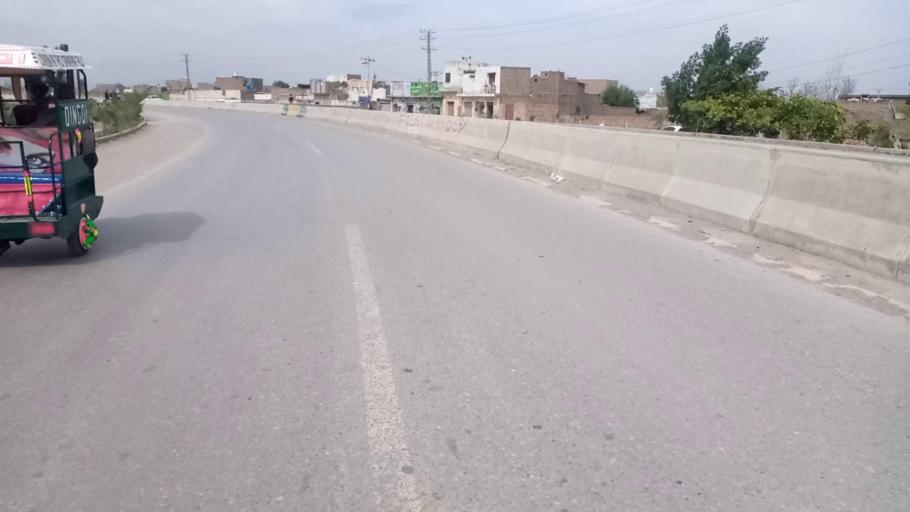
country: PK
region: Khyber Pakhtunkhwa
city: Peshawar
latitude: 34.0332
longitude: 71.6422
